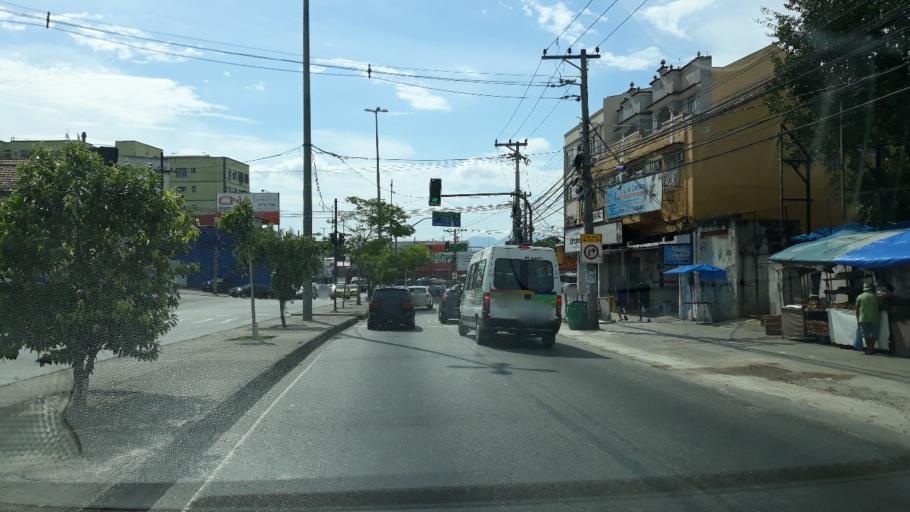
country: BR
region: Rio de Janeiro
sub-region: Sao Joao De Meriti
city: Sao Joao de Meriti
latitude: -22.8824
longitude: -43.3239
